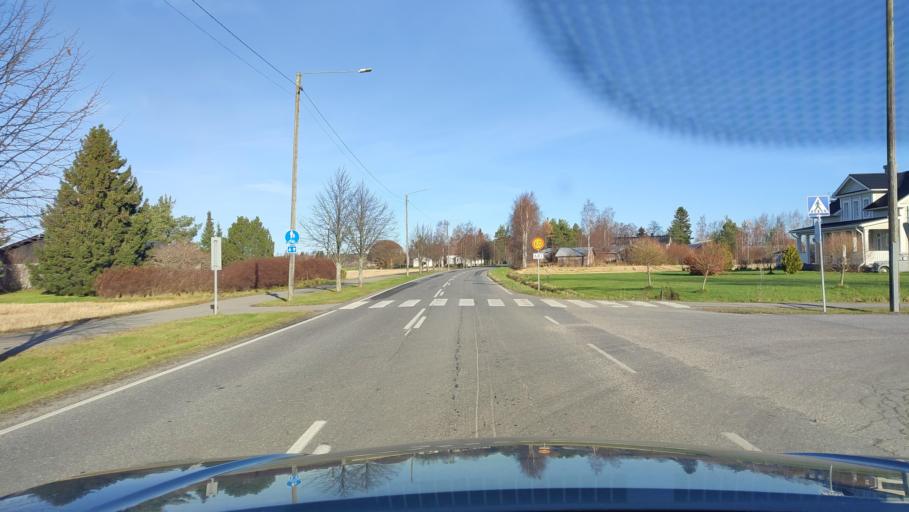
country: FI
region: Southern Ostrobothnia
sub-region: Suupohja
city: Teuva
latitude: 62.4695
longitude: 21.7119
